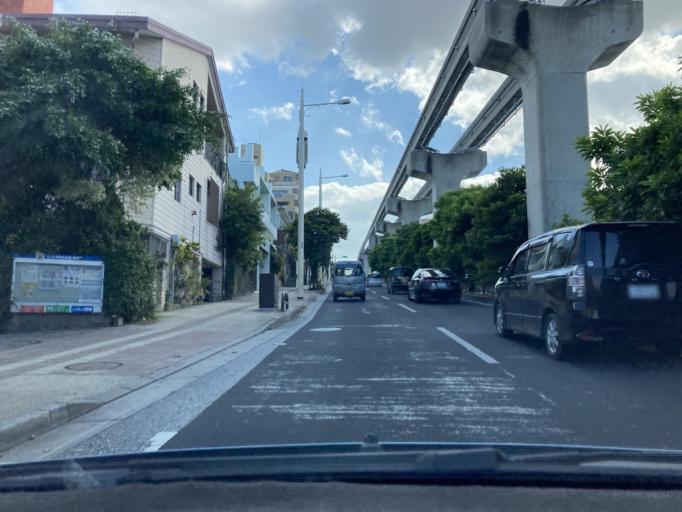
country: JP
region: Okinawa
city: Naha-shi
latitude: 26.2229
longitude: 127.7210
